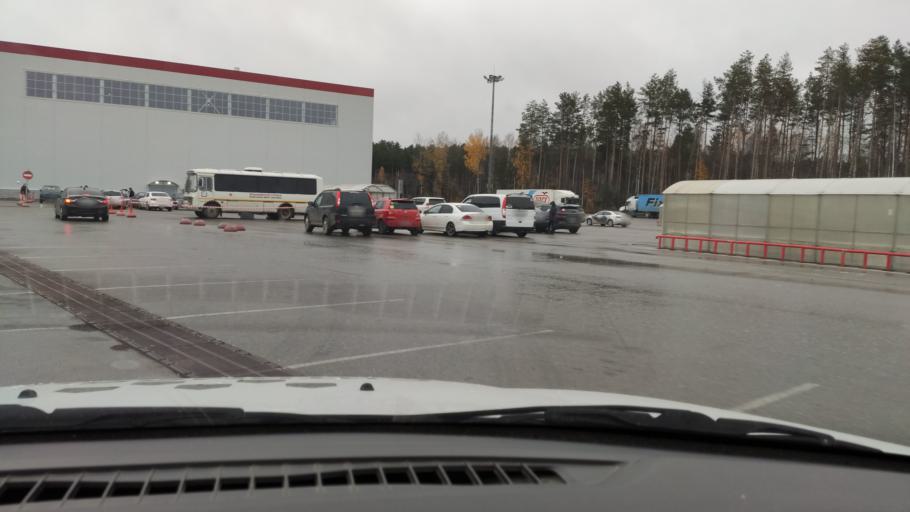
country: RU
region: Perm
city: Perm
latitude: 58.0394
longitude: 56.1939
